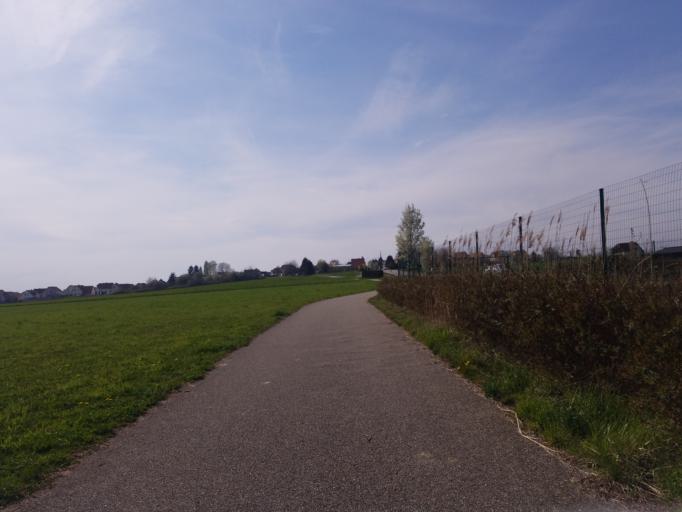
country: FR
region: Alsace
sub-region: Departement du Bas-Rhin
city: Betschdorf
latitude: 48.9023
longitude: 7.9667
